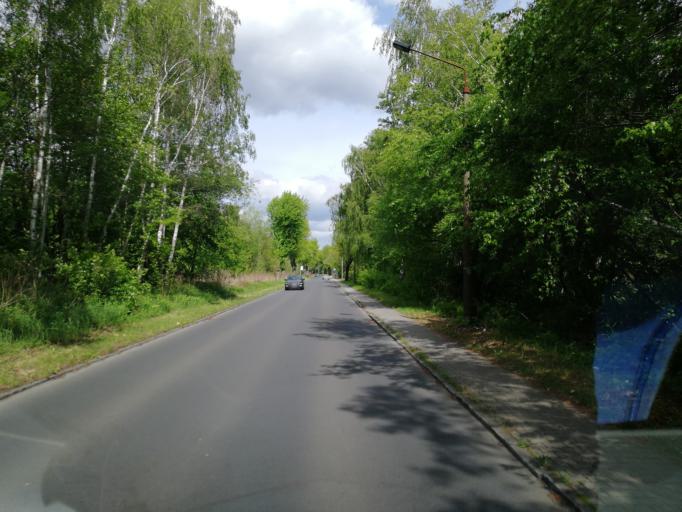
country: DE
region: Brandenburg
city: Lauchhammer
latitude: 51.4873
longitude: 13.7501
